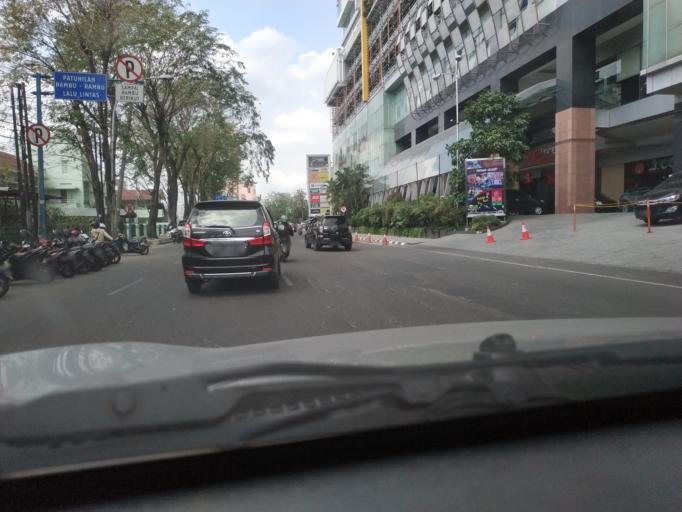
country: ID
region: North Sumatra
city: Medan
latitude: 3.5845
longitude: 98.6669
